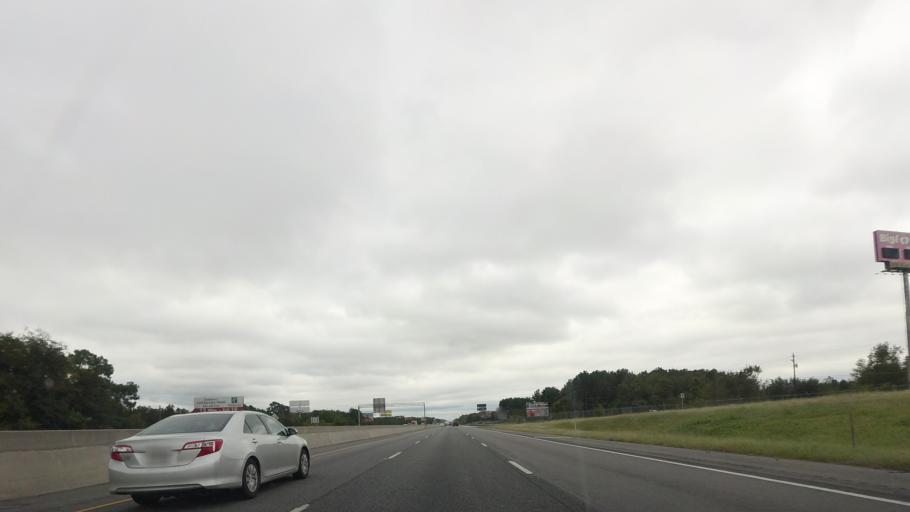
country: US
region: Georgia
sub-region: Lowndes County
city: Hahira
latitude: 30.9913
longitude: -83.3878
